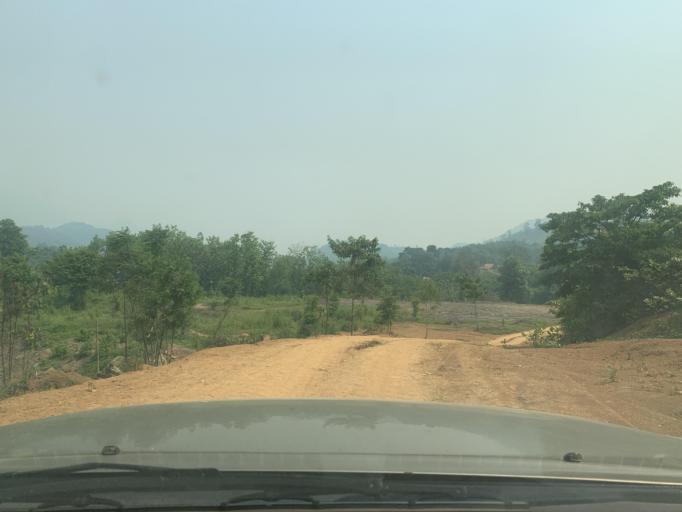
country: LA
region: Louangphabang
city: Xiang Ngeun
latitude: 19.8004
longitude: 102.2023
